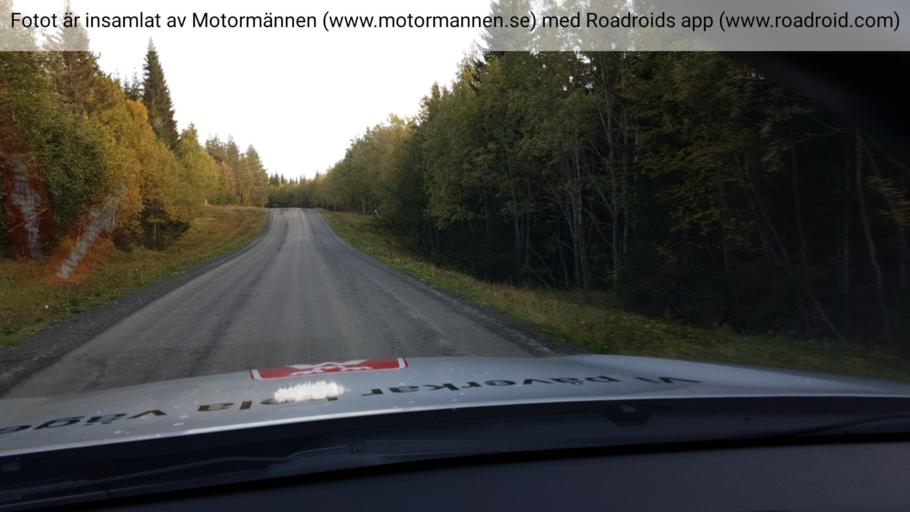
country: SE
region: Jaemtland
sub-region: Krokoms Kommun
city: Krokom
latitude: 63.7543
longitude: 14.4437
